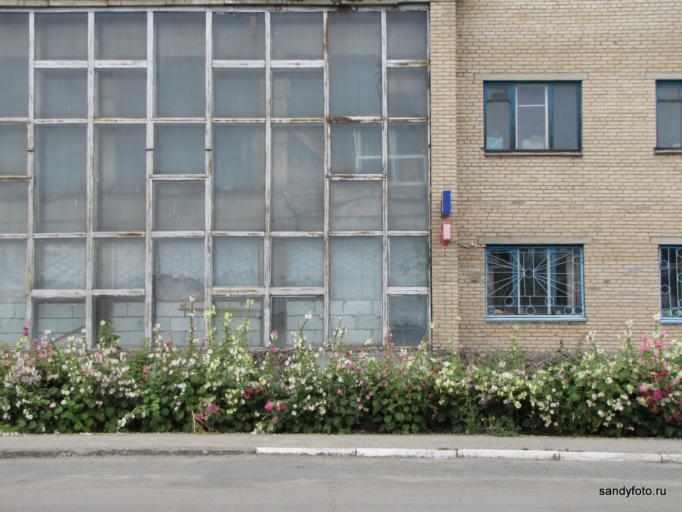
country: RU
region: Chelyabinsk
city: Troitsk
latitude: 54.0837
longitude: 61.5612
